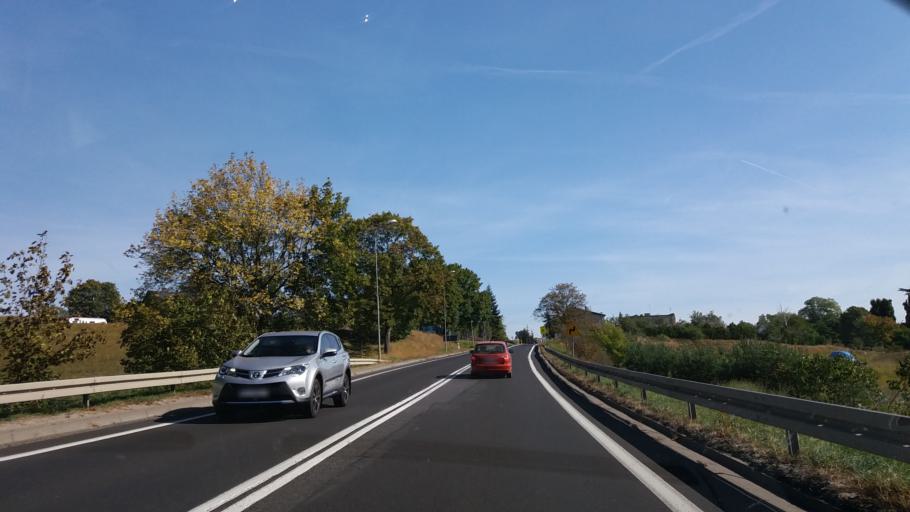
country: PL
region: Greater Poland Voivodeship
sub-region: Powiat miedzychodzki
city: Miedzychod
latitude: 52.5659
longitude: 15.9528
